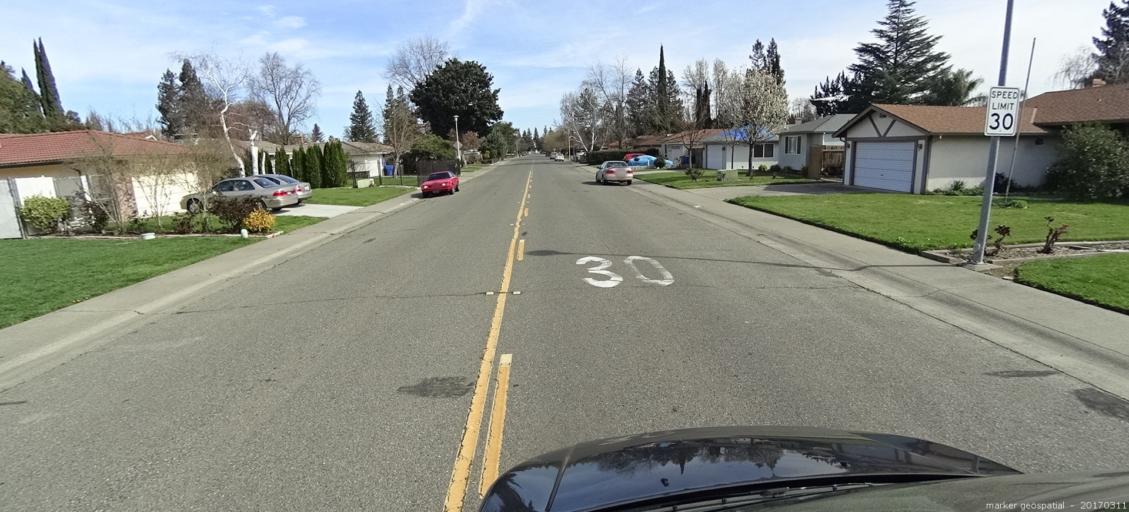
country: US
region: California
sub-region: Yolo County
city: West Sacramento
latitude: 38.5015
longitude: -121.5543
